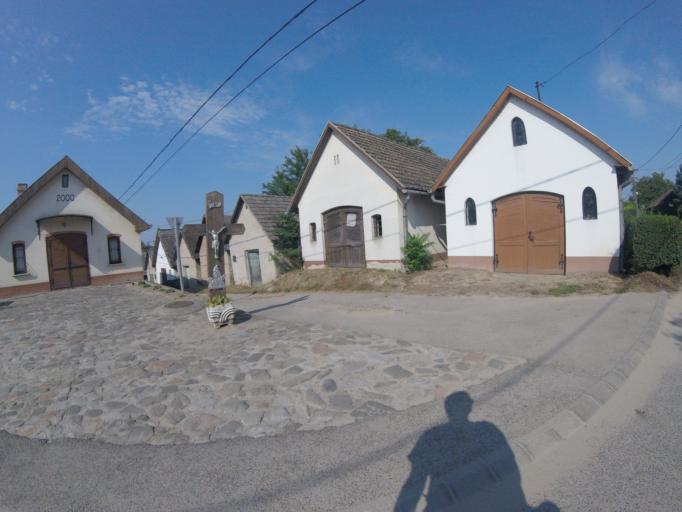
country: HU
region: Tolna
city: Dunafoldvar
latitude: 46.8152
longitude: 18.9192
